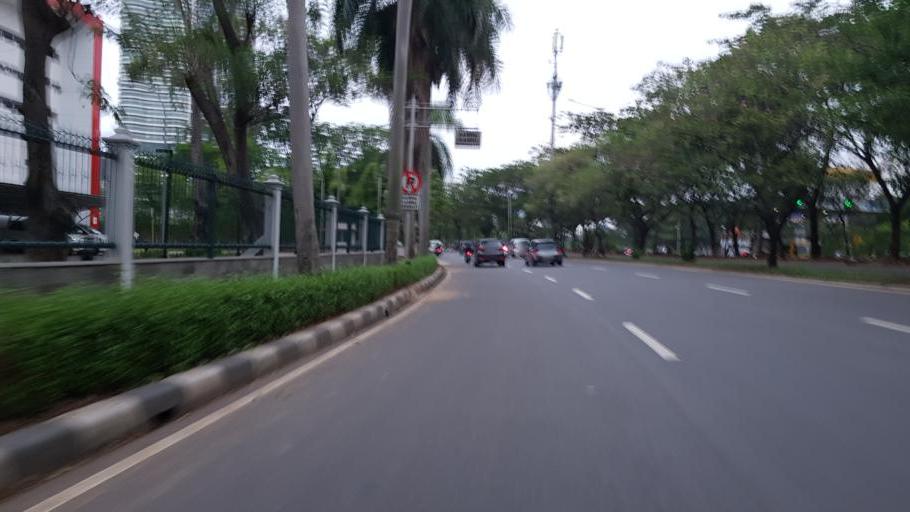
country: ID
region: West Java
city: Ciputat
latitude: -6.1908
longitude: 106.7354
